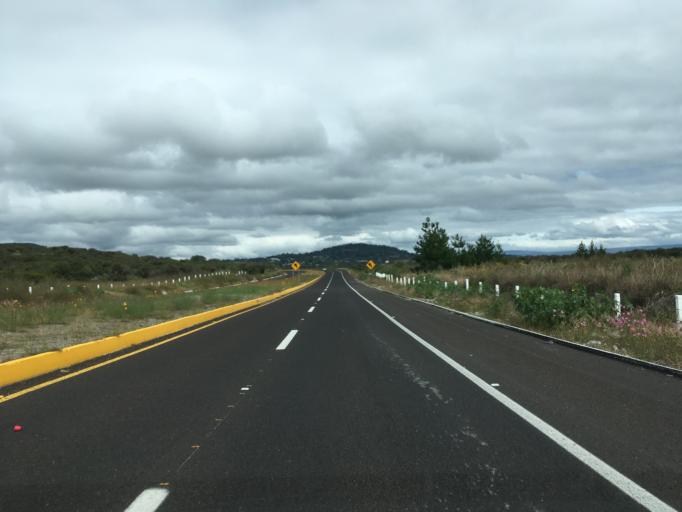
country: MX
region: Hidalgo
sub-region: Atotonilco el Grande
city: Santa Maria Amajac
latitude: 20.3732
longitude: -98.7201
